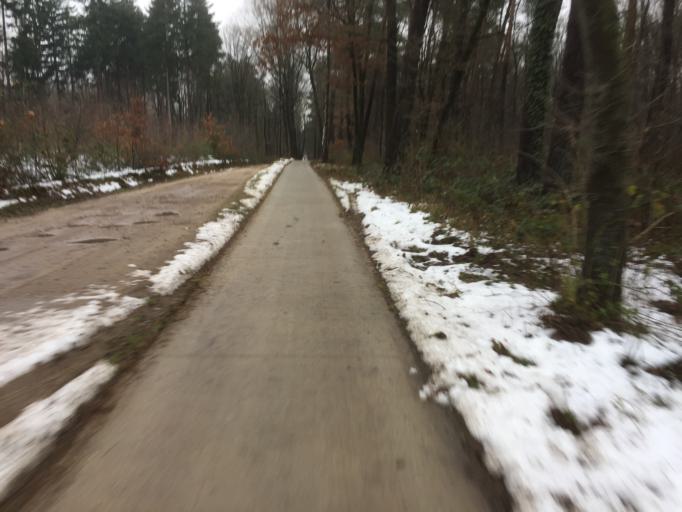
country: NL
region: Gelderland
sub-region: Gemeente Ede
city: Bennekom
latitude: 52.0227
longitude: 5.6952
